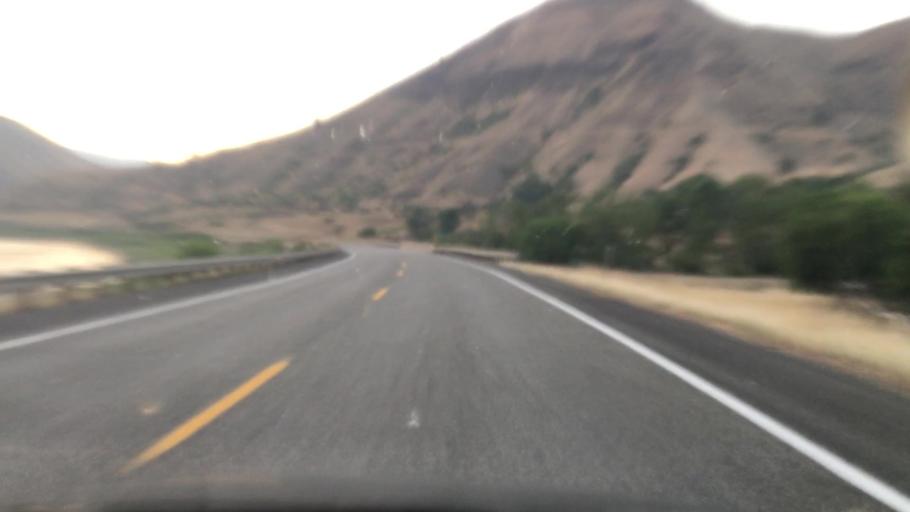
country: US
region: Idaho
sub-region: Idaho County
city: Grangeville
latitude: 45.6391
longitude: -116.2830
